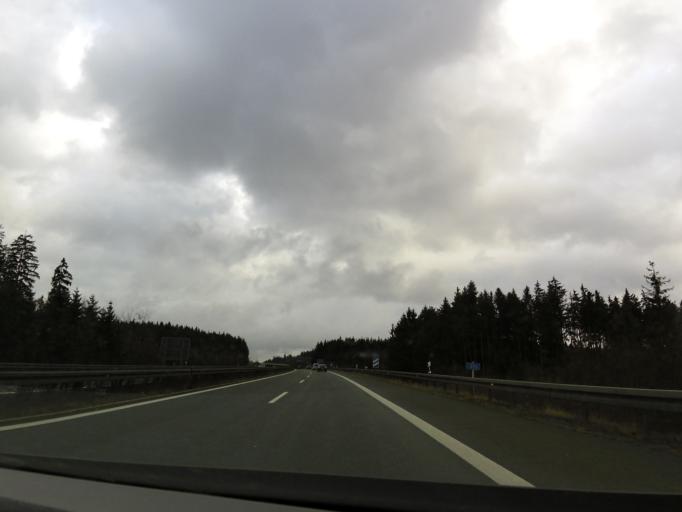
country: DE
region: Bavaria
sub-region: Upper Franconia
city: Rehau
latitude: 50.2725
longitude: 12.0264
